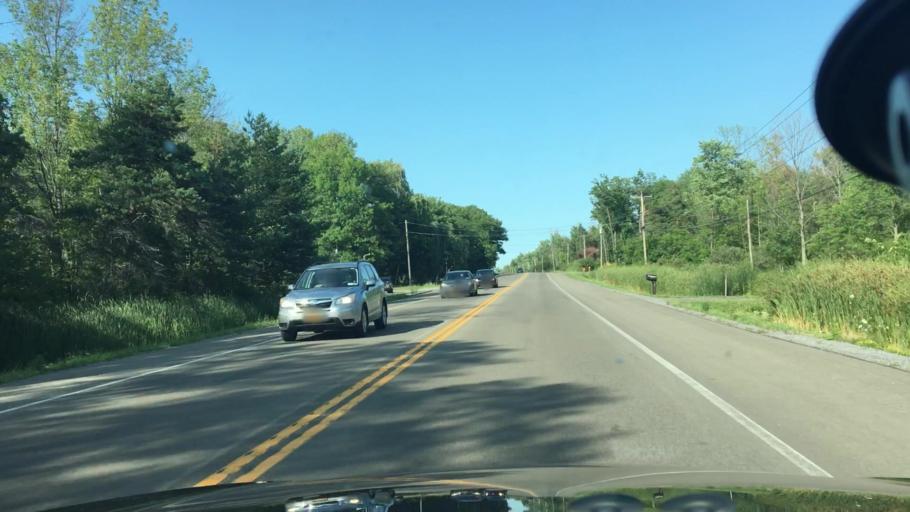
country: US
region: New York
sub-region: Erie County
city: Wanakah
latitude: 42.6993
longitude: -78.9322
